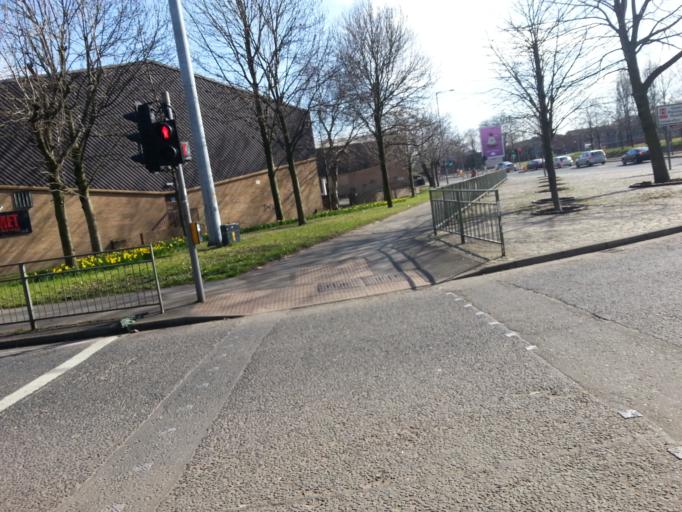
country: GB
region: England
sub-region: Manchester
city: Manchester
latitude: 53.4740
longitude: -2.2295
